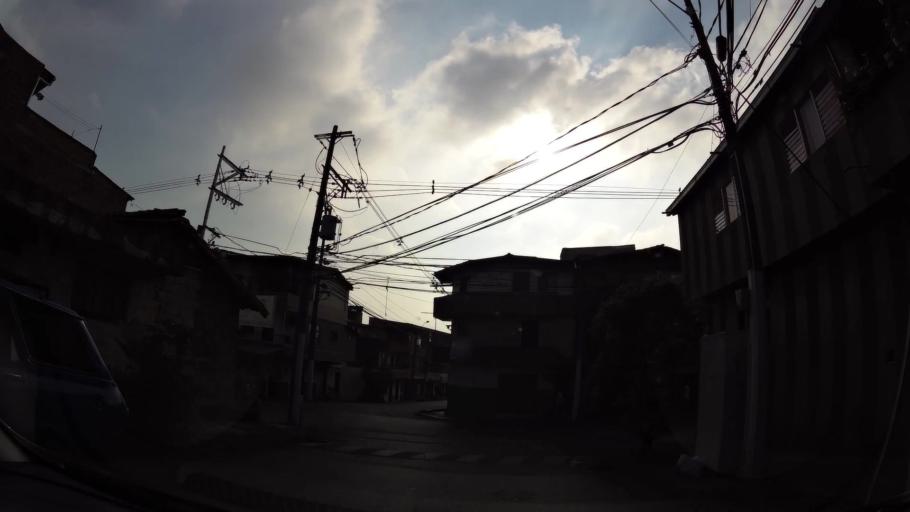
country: CO
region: Antioquia
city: Sabaneta
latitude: 6.1622
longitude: -75.6241
